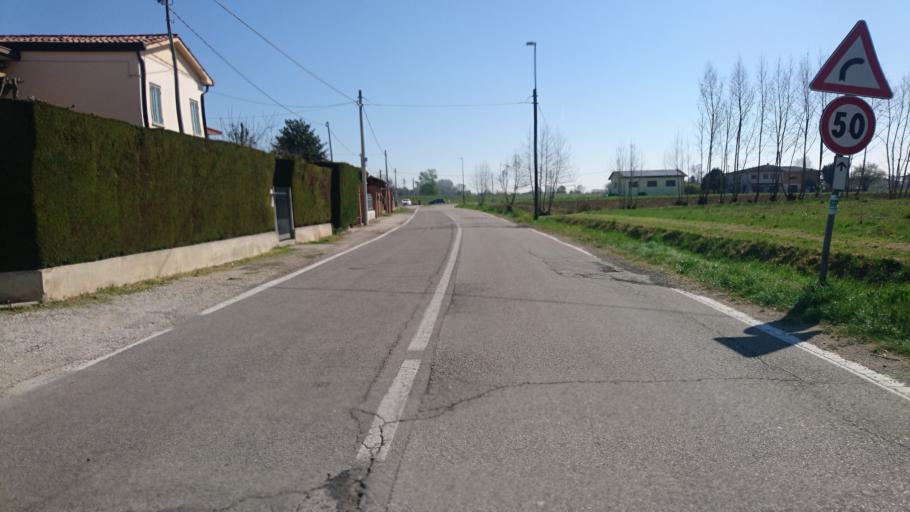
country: IT
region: Veneto
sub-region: Provincia di Padova
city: Ponte San Nicolo
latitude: 45.3798
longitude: 11.9182
